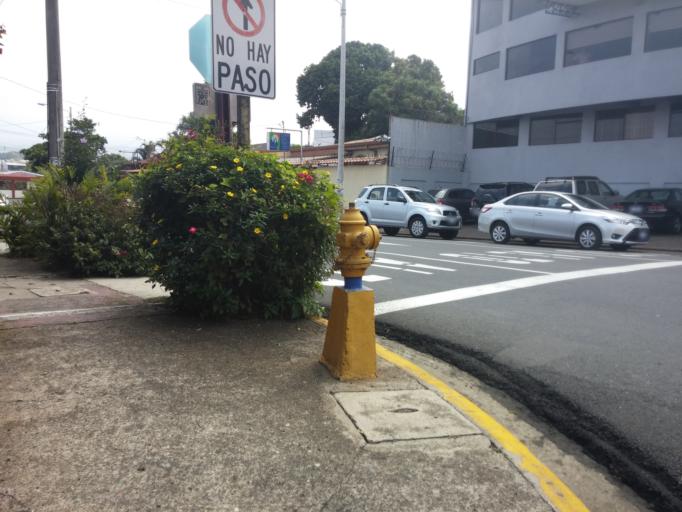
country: CR
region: Heredia
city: Heredia
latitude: 10.0003
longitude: -84.1236
